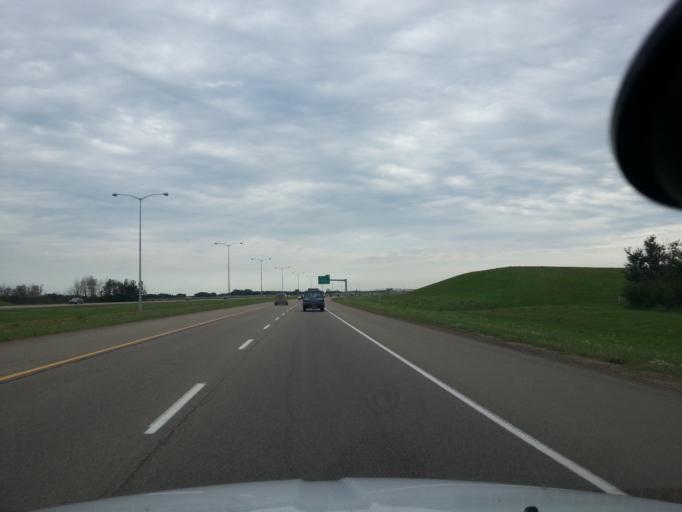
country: CA
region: Alberta
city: Edmonton
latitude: 53.6456
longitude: -113.5207
